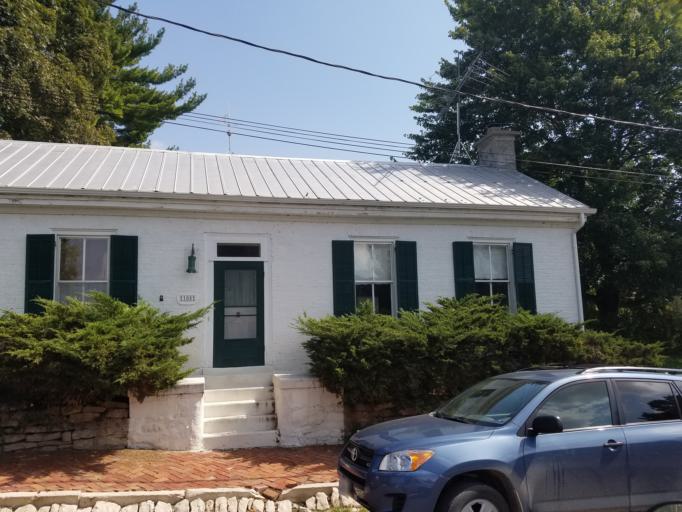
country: US
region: Missouri
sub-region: Howard County
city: New Franklin
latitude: 38.9788
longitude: -92.5665
